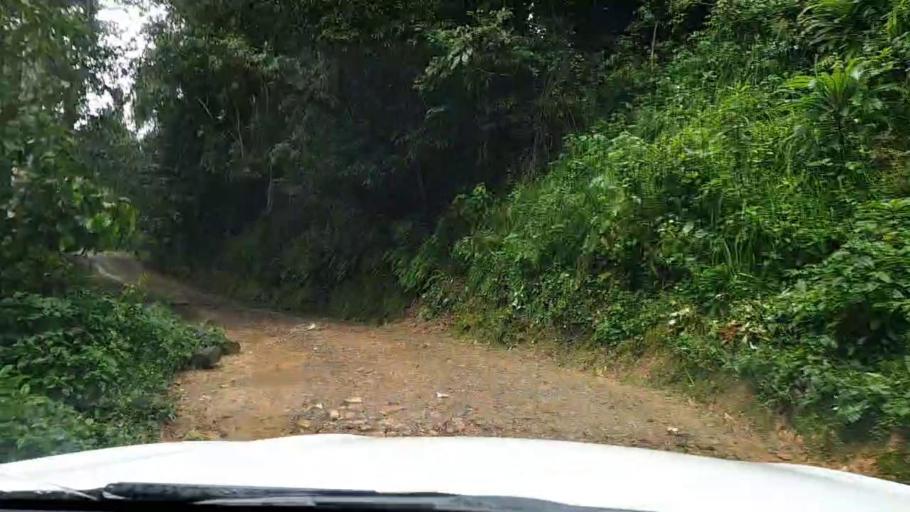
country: RW
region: Western Province
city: Cyangugu
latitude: -2.5586
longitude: 28.9815
